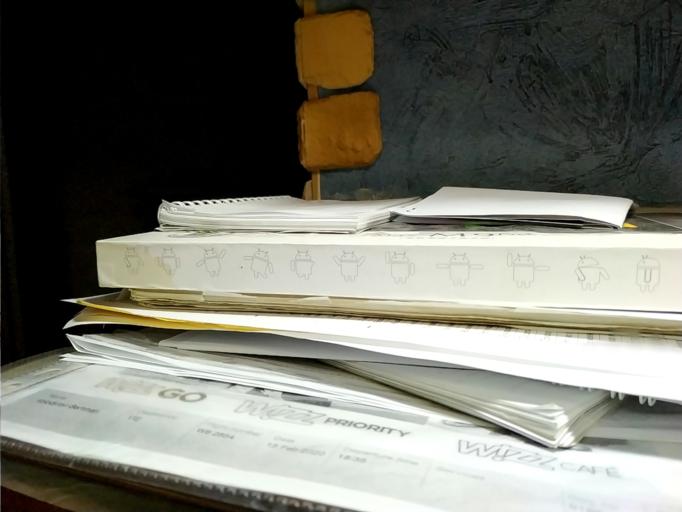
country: RU
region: Arkhangelskaya
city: Onega
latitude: 63.3665
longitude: 38.2243
